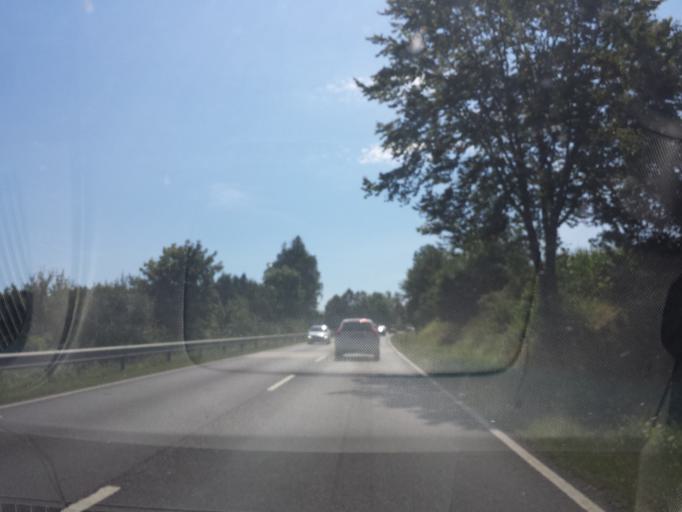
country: DE
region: Bavaria
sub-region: Upper Palatinate
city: Traitsching
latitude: 49.1299
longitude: 12.6531
